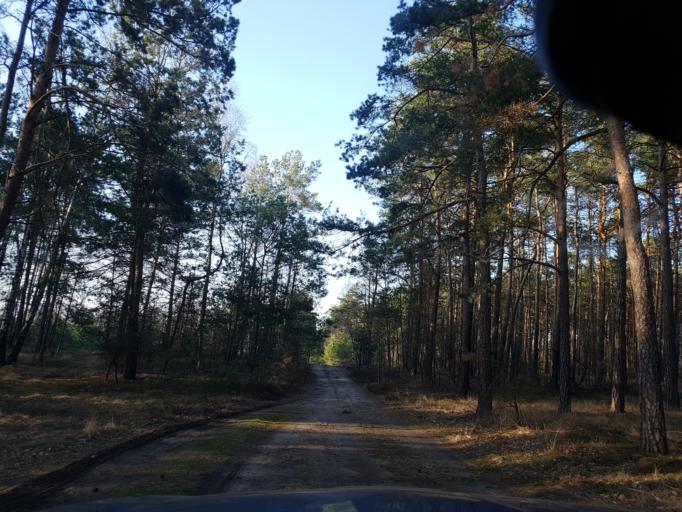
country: DE
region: Brandenburg
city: Schonewalde
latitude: 51.6349
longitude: 13.6158
